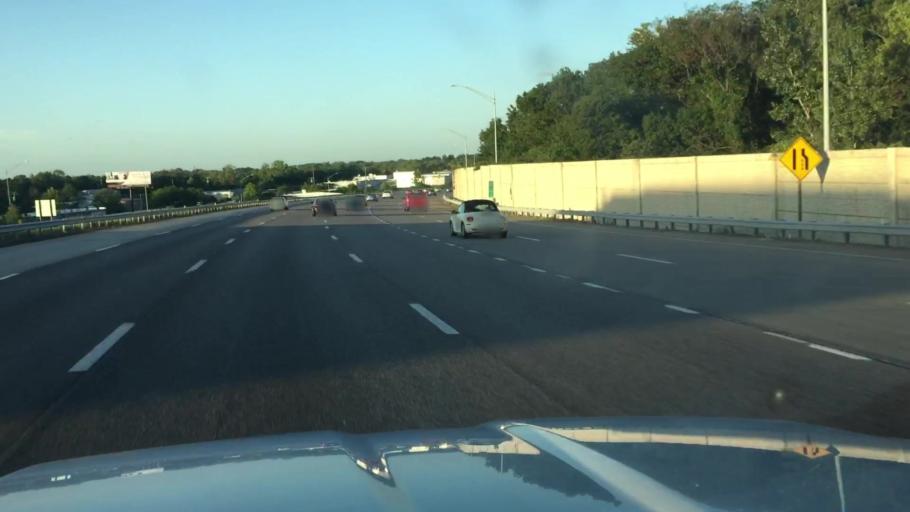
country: US
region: Missouri
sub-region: Saint Louis County
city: Green Park
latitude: 38.5170
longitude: -90.3329
